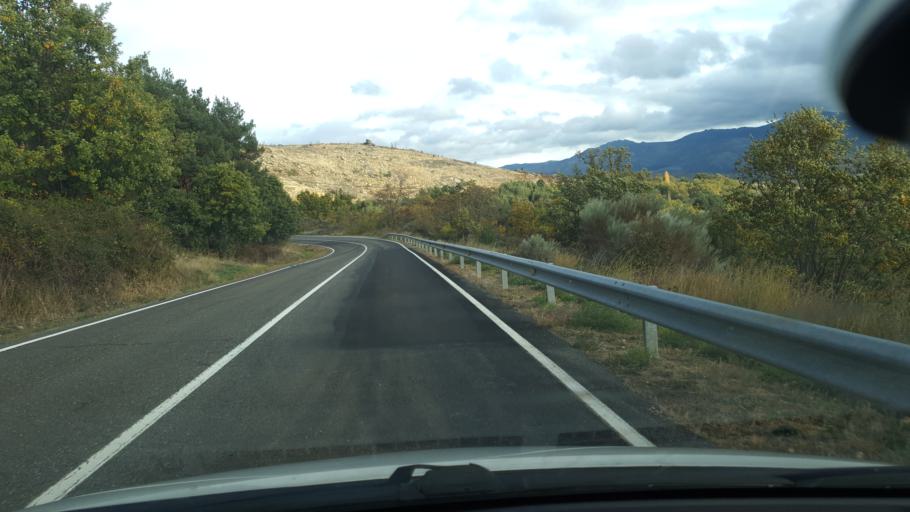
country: ES
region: Castille and Leon
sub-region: Provincia de Avila
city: Hoyocasero
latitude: 40.3973
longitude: -4.9711
